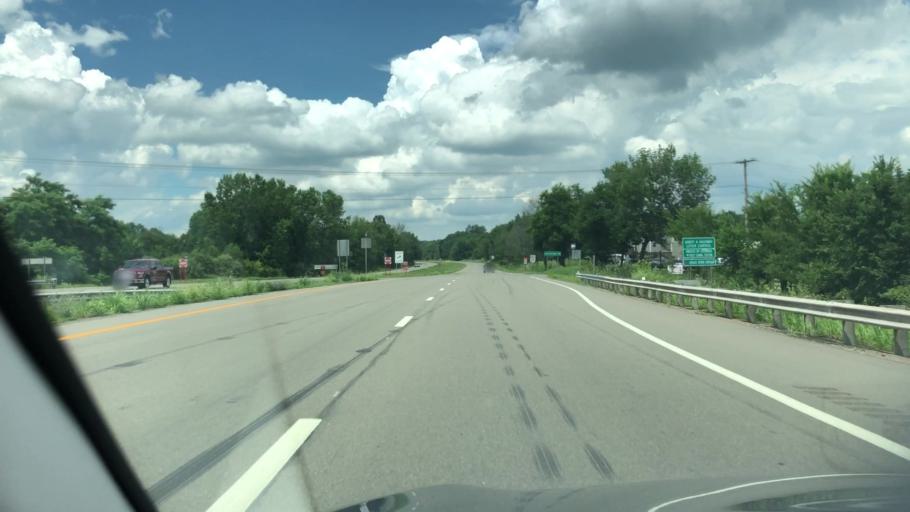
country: US
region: Ohio
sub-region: Stark County
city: Canal Fulton
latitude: 40.8570
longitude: -81.5786
